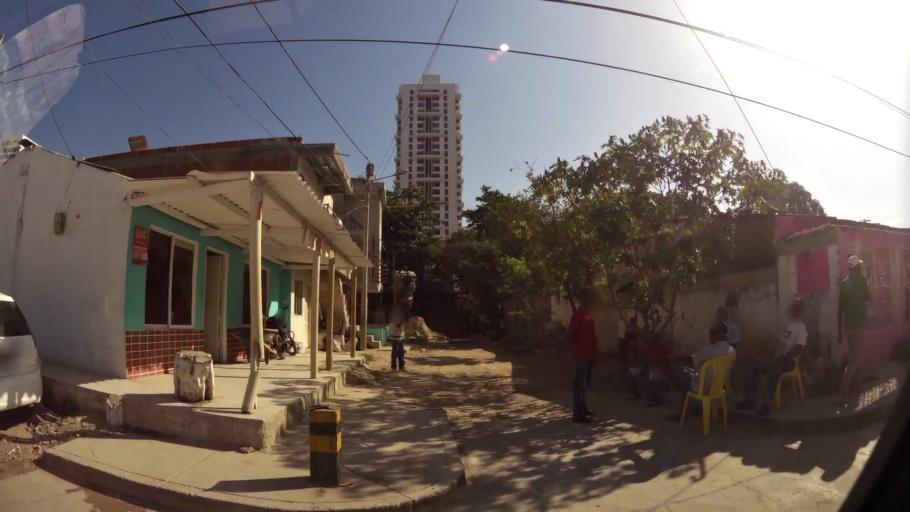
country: CO
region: Bolivar
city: Cartagena
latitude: 10.4330
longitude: -75.5354
